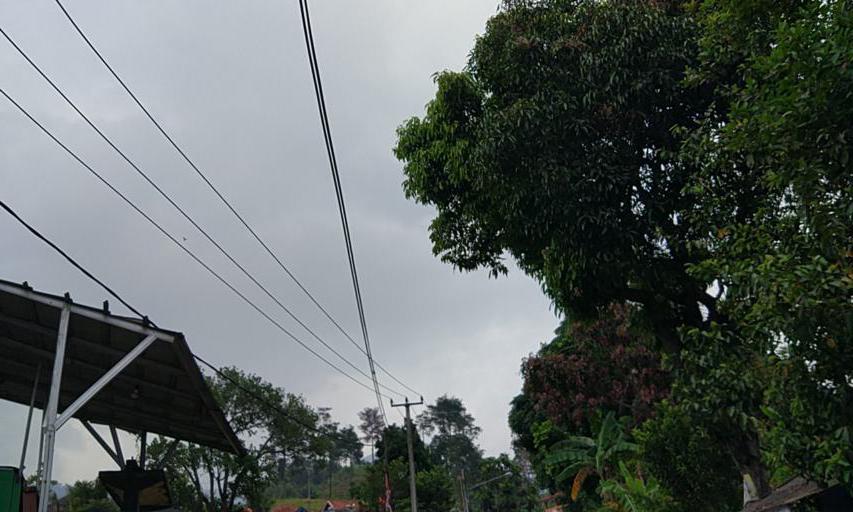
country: ID
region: West Java
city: Bandung
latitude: -6.8867
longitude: 107.6869
